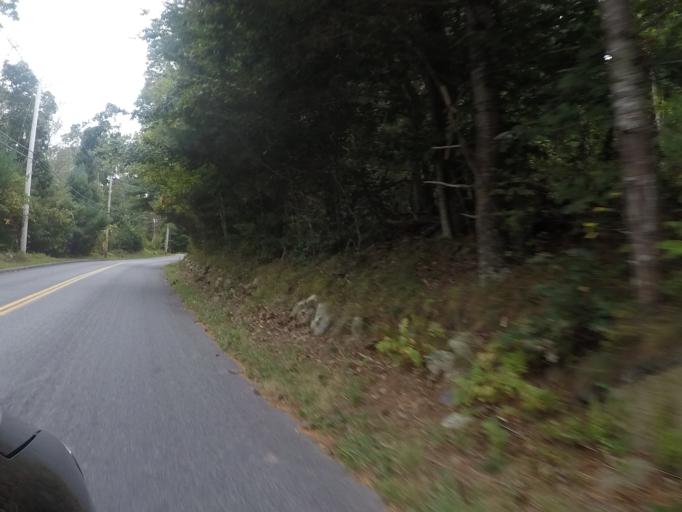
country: US
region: Massachusetts
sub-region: Bristol County
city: Smith Mills
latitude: 41.5618
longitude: -71.0077
